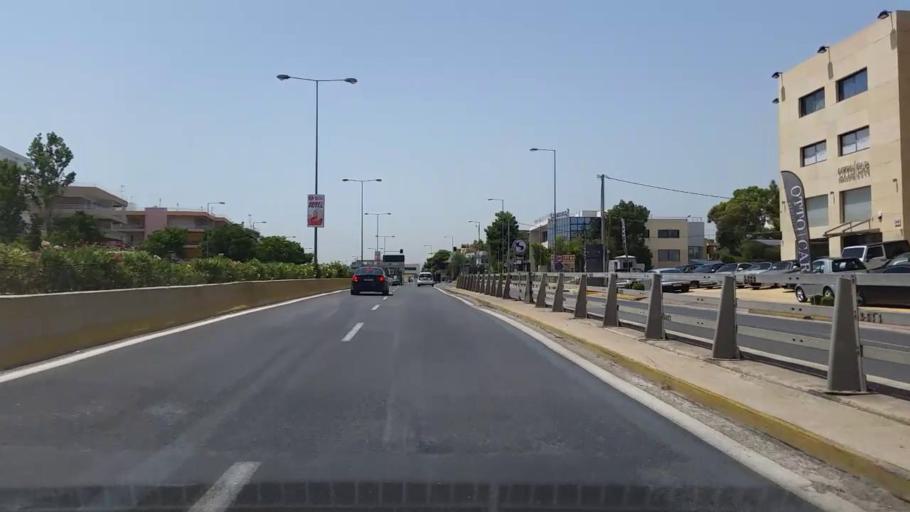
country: GR
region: Attica
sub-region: Nomarchia Athinas
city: Agia Paraskevi
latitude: 38.0116
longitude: 23.8386
